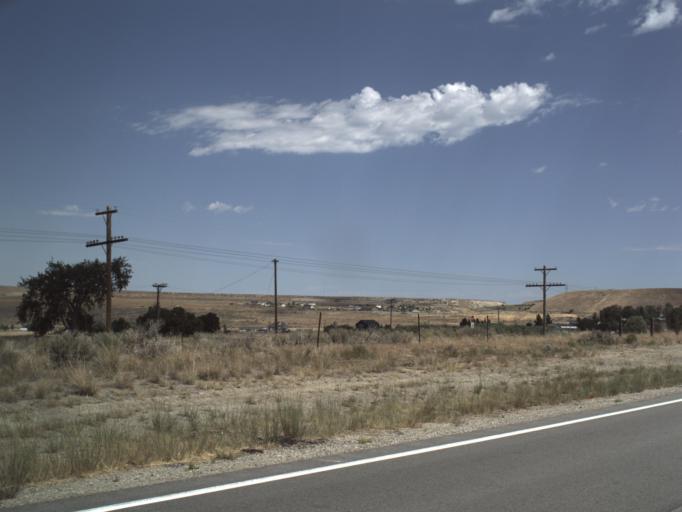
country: US
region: Utah
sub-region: Tooele County
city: Tooele
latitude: 40.4396
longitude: -112.3708
